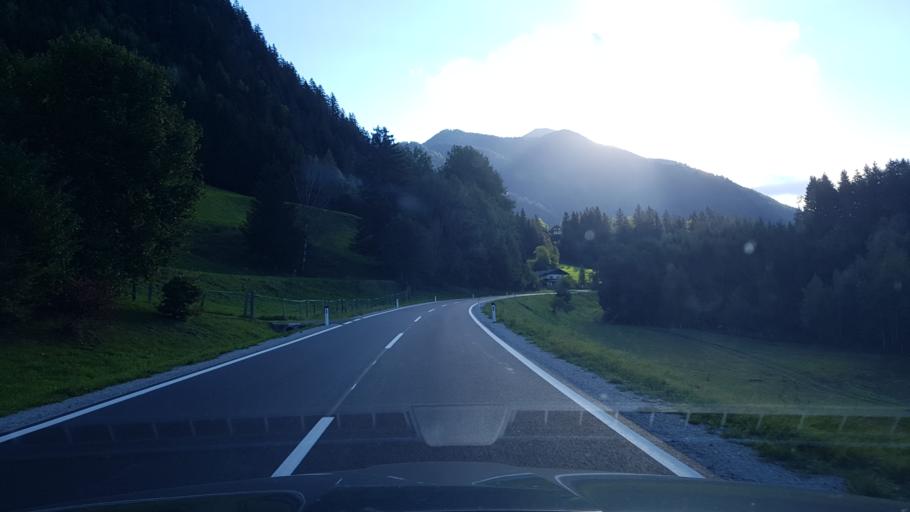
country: AT
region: Styria
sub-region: Politischer Bezirk Liezen
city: Grosssolk
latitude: 47.4141
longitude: 13.9598
